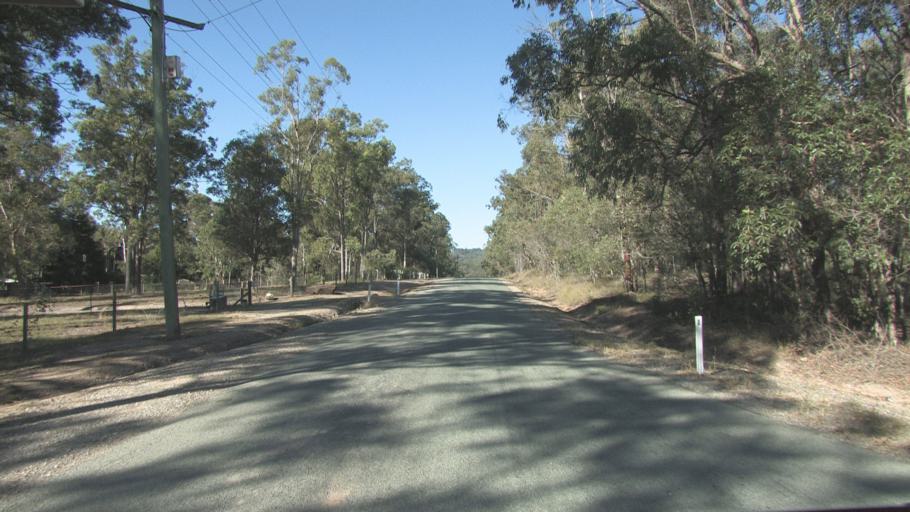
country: AU
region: Queensland
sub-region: Logan
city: Chambers Flat
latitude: -27.7628
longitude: 153.1336
